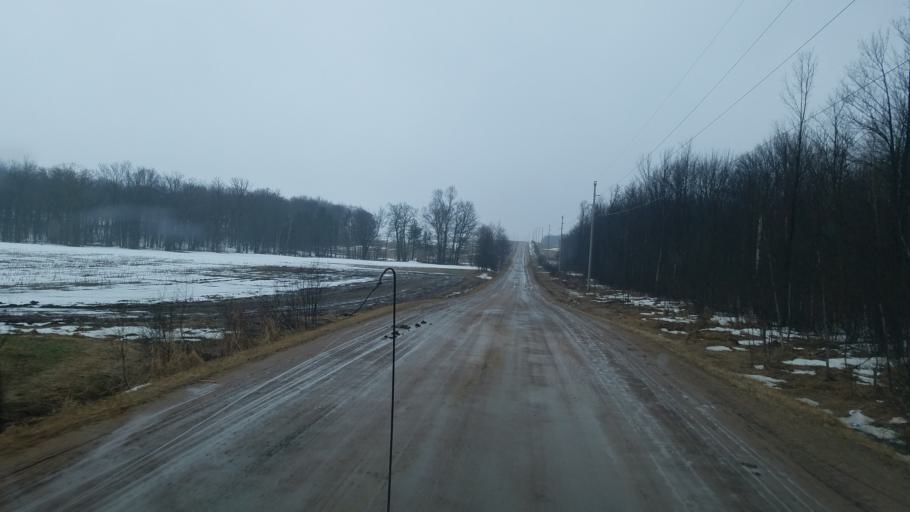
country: US
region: Wisconsin
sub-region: Clark County
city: Loyal
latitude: 44.6060
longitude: -90.3967
